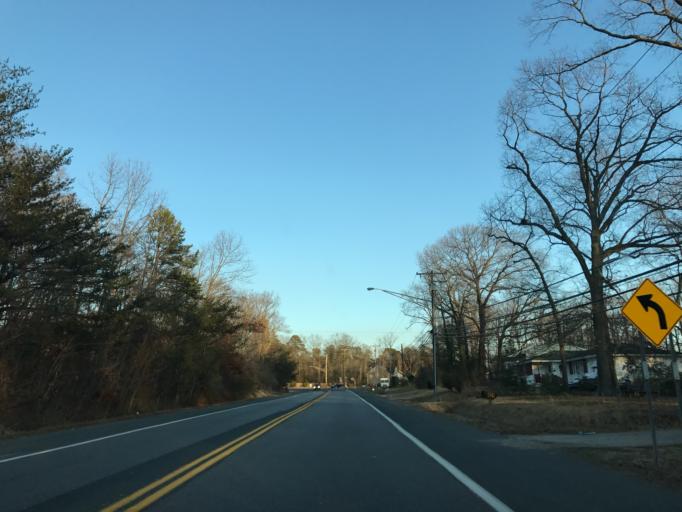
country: US
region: Maryland
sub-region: Anne Arundel County
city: Green Haven
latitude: 39.1098
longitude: -76.5290
